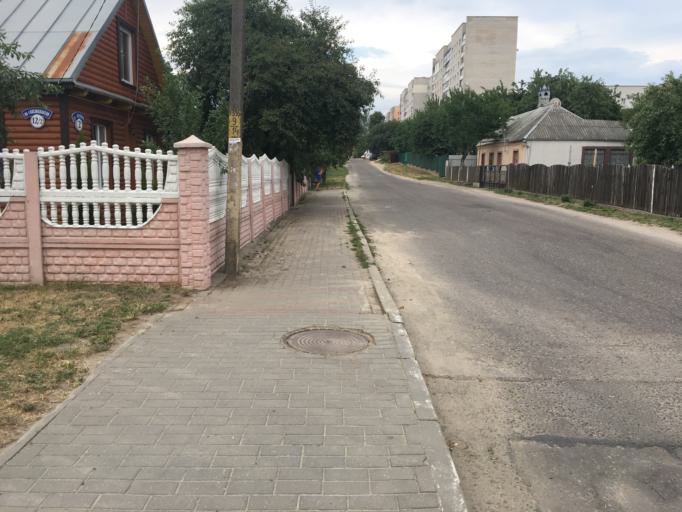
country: BY
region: Grodnenskaya
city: Hrodna
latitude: 53.6751
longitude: 23.8550
